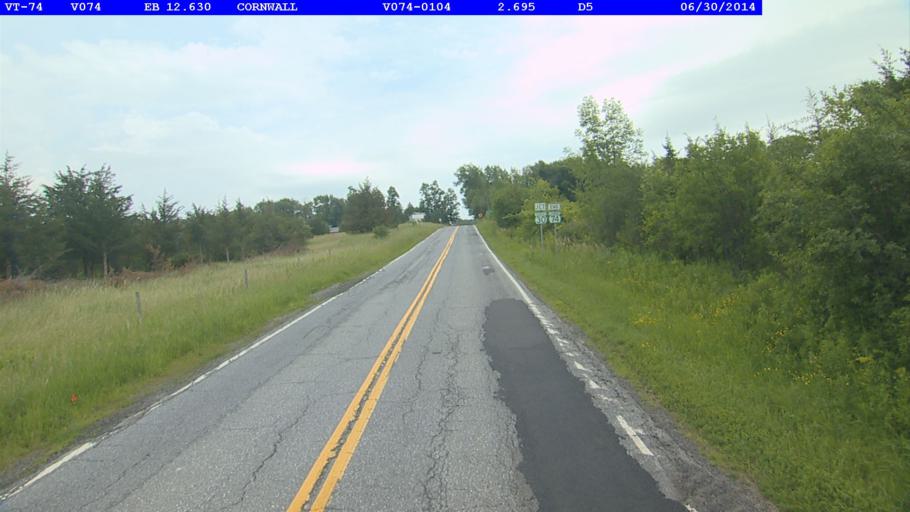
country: US
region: Vermont
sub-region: Addison County
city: Middlebury (village)
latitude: 43.9589
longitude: -73.2127
